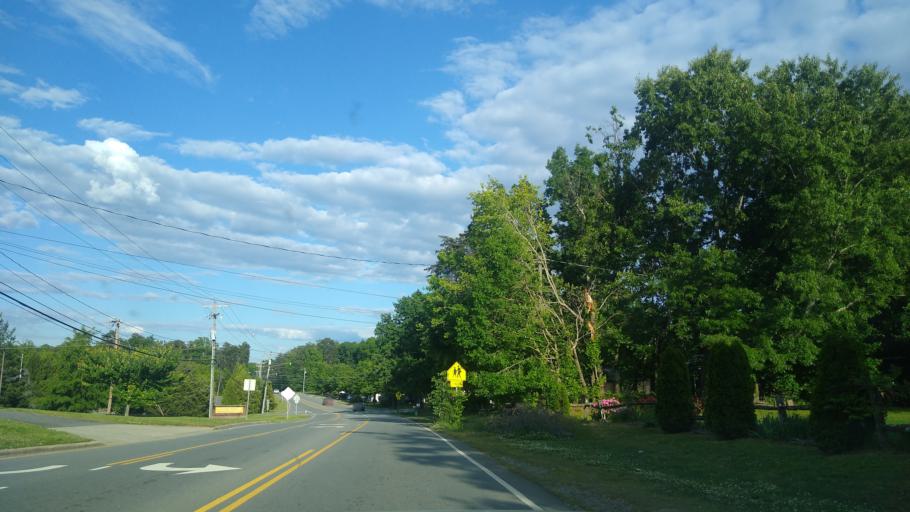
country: US
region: North Carolina
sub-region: Guilford County
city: Greensboro
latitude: 36.1475
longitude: -79.7536
